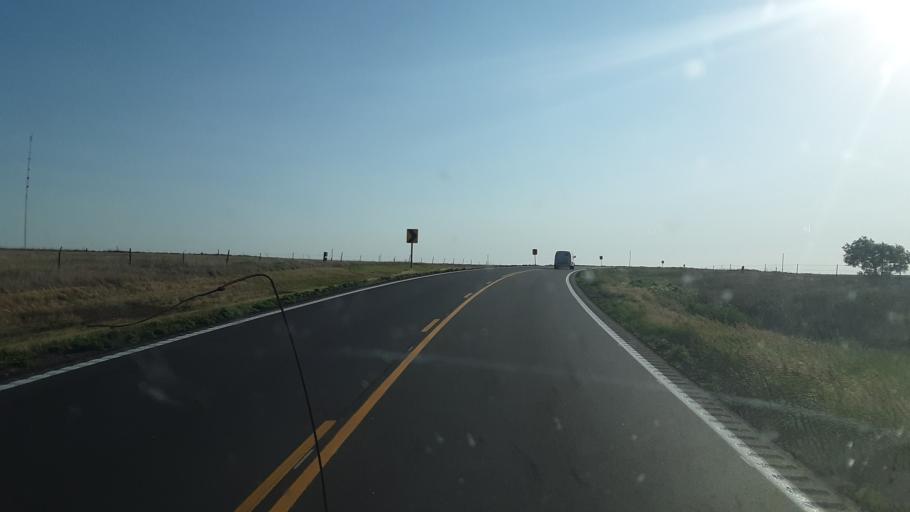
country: US
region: Kansas
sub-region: Hodgeman County
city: Jetmore
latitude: 38.0861
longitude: -99.9760
